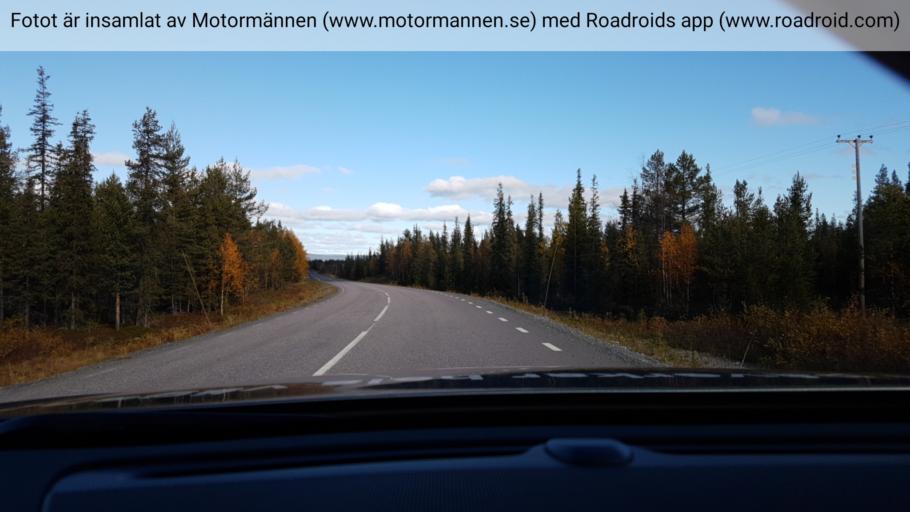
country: SE
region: Norrbotten
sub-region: Gallivare Kommun
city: Gaellivare
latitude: 67.0639
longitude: 20.7428
